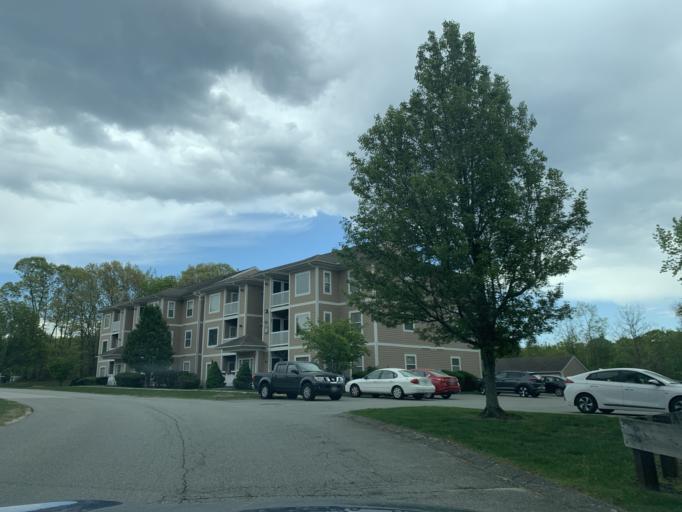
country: US
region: Rhode Island
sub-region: Kent County
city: West Warwick
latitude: 41.6707
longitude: -71.4935
